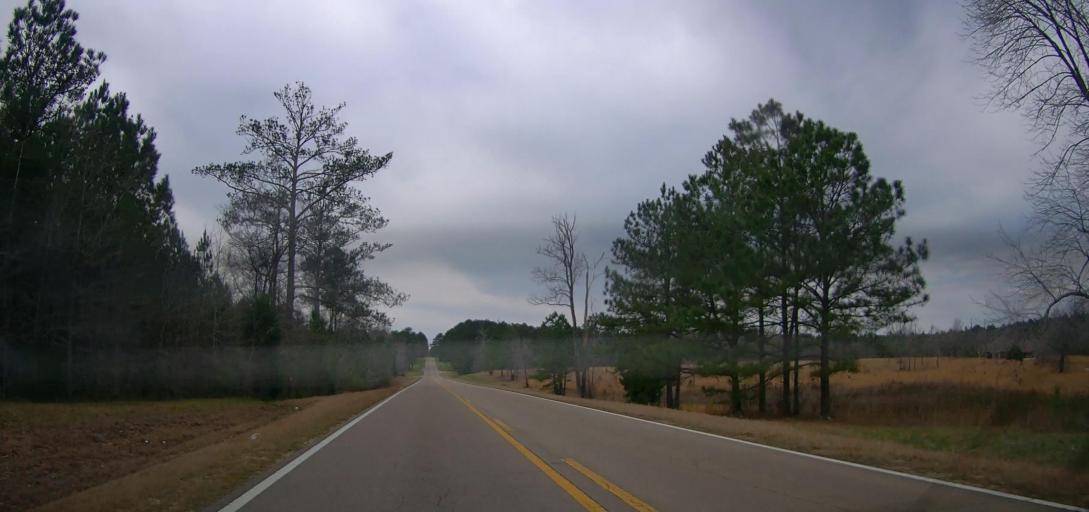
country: US
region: Mississippi
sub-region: Itawamba County
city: Mantachie
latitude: 34.2625
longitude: -88.5320
